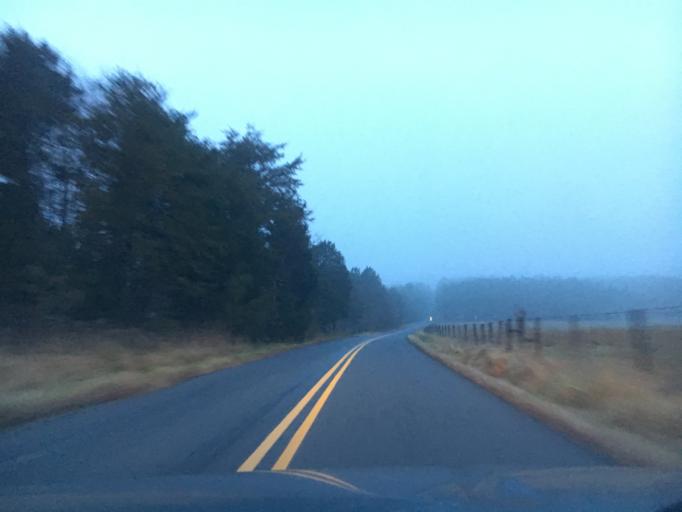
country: US
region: Virginia
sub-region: Halifax County
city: Mountain Road
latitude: 36.6817
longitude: -79.0303
